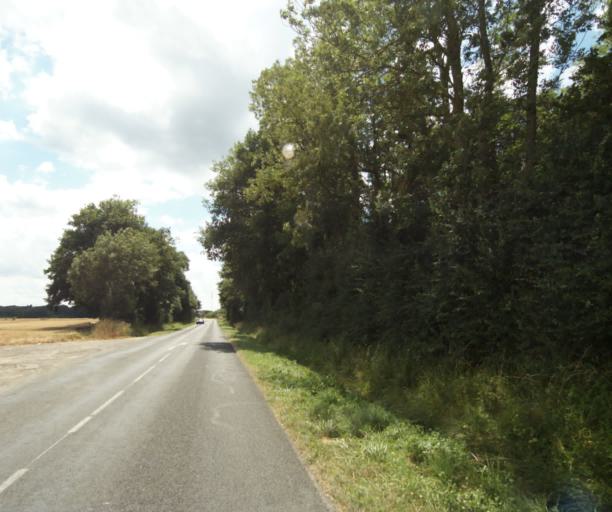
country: FR
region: Ile-de-France
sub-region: Departement de Seine-et-Marne
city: Vulaines-sur-Seine
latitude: 48.4378
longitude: 2.7736
